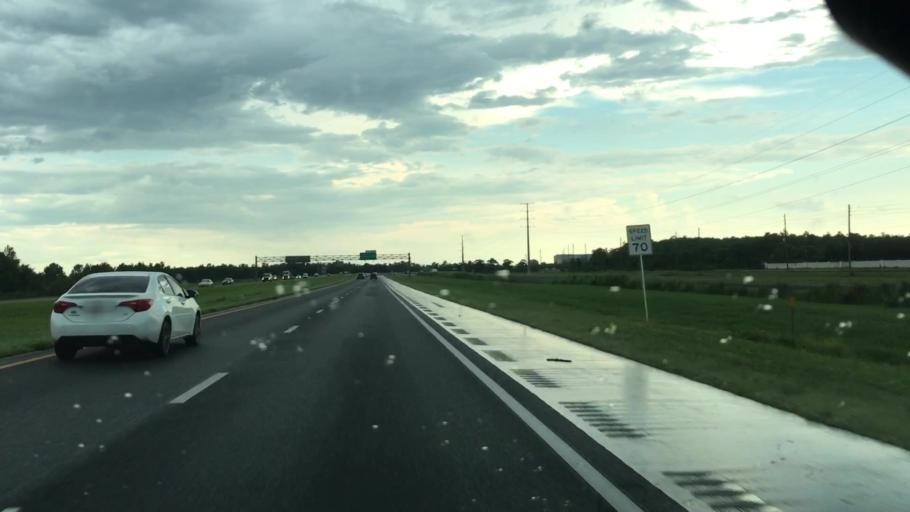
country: US
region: Florida
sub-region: Orange County
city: Meadow Woods
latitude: 28.3911
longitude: -81.2551
